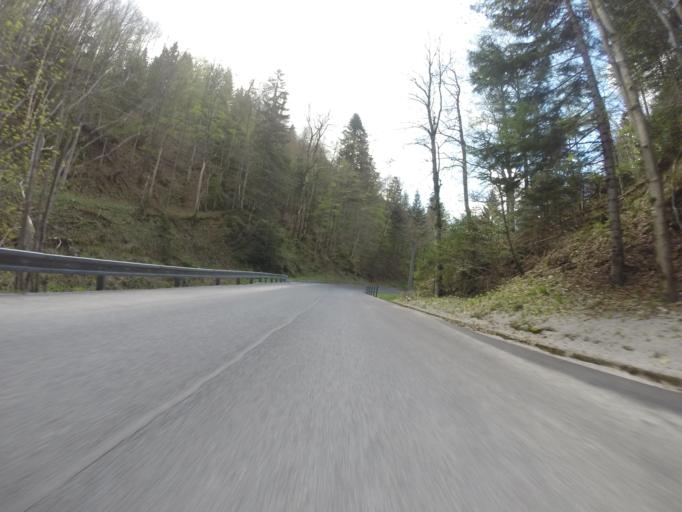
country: SK
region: Banskobystricky
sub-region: Okres Banska Bystrica
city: Brezno
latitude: 48.9125
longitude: 19.6000
